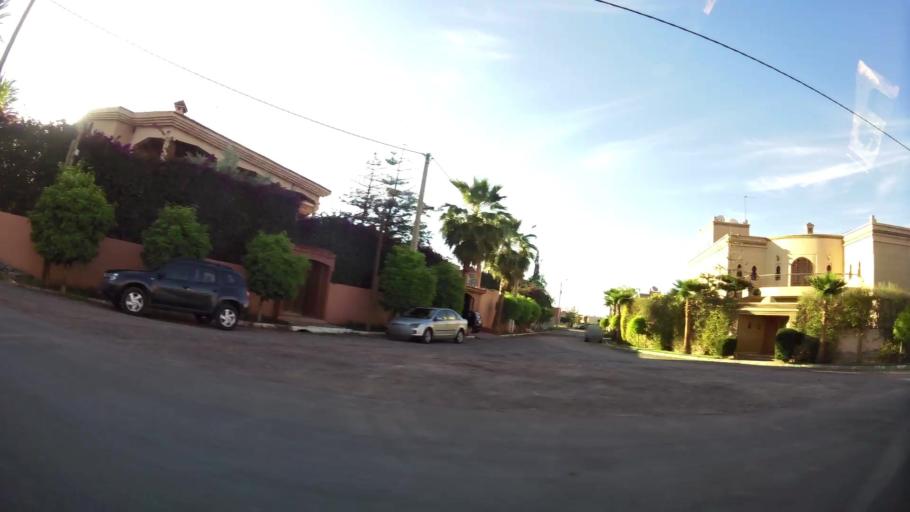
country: MA
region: Marrakech-Tensift-Al Haouz
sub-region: Marrakech
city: Marrakesh
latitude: 31.6650
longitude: -8.0598
